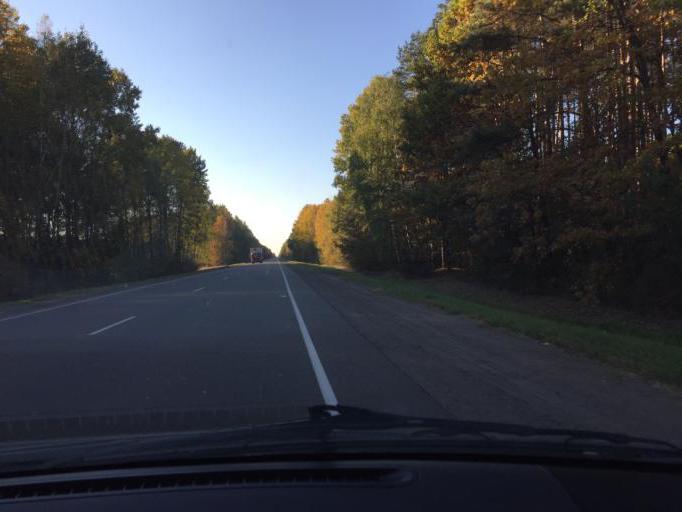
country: BY
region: Brest
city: Horad Luninyets
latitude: 52.2927
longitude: 26.7637
